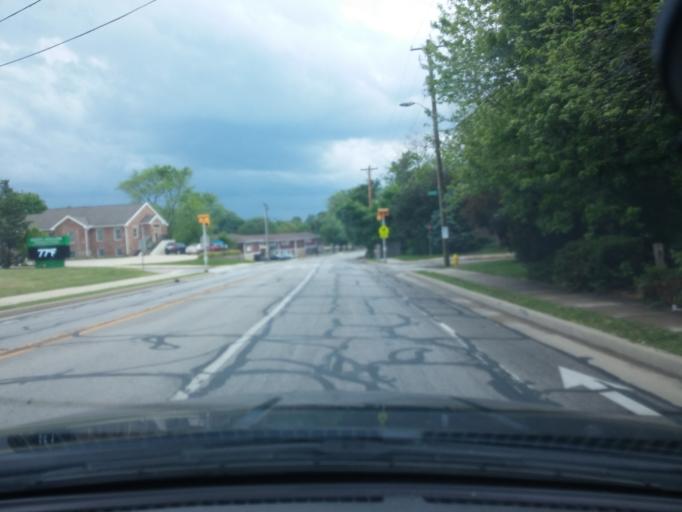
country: US
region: Indiana
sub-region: Tippecanoe County
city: West Lafayette
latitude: 40.4372
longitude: -86.9062
